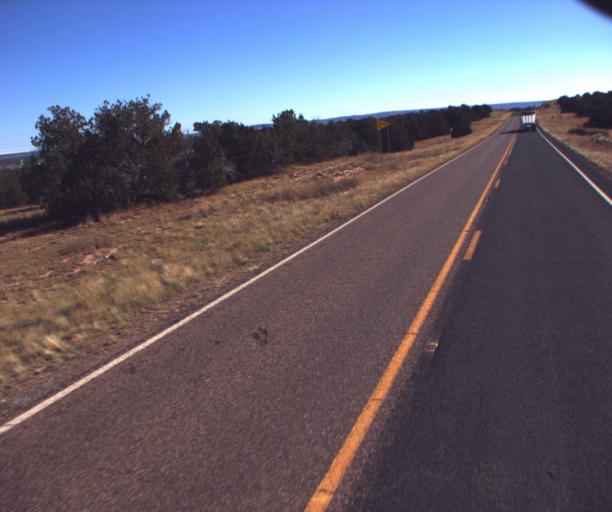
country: US
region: Arizona
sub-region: Apache County
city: Ganado
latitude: 35.4450
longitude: -109.5221
